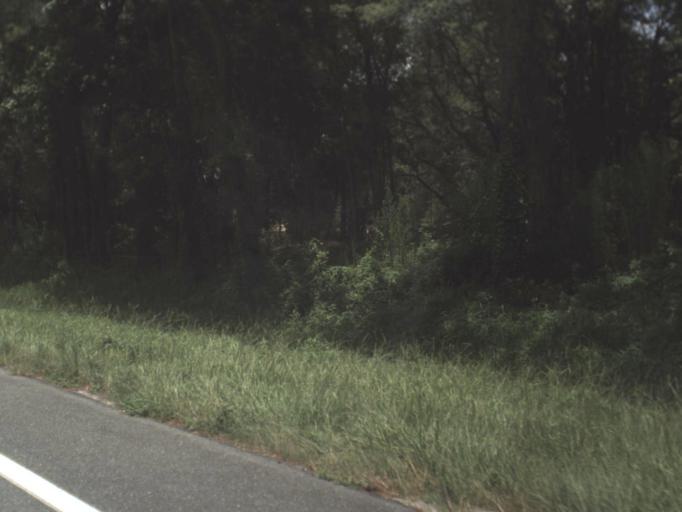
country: US
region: Florida
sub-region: Columbia County
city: Five Points
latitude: 30.2832
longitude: -82.7014
